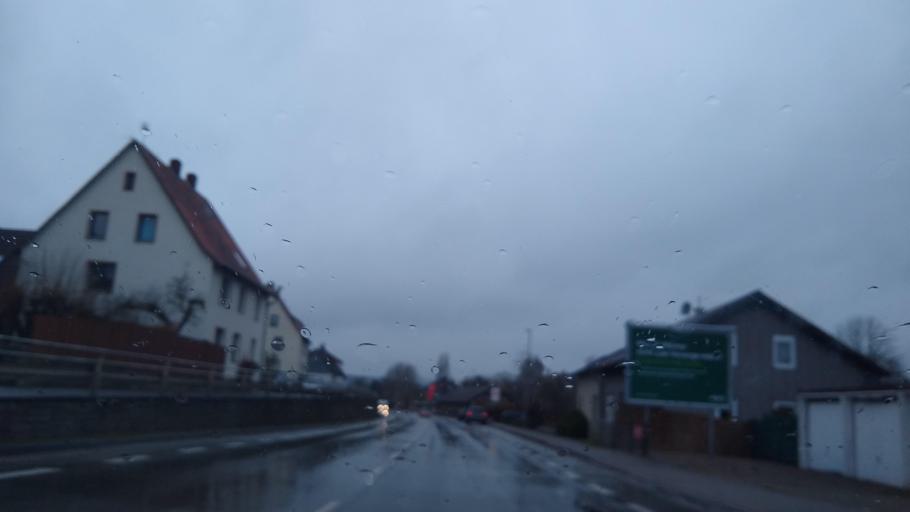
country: DE
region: Lower Saxony
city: Hehlen
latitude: 51.9852
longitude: 9.4770
